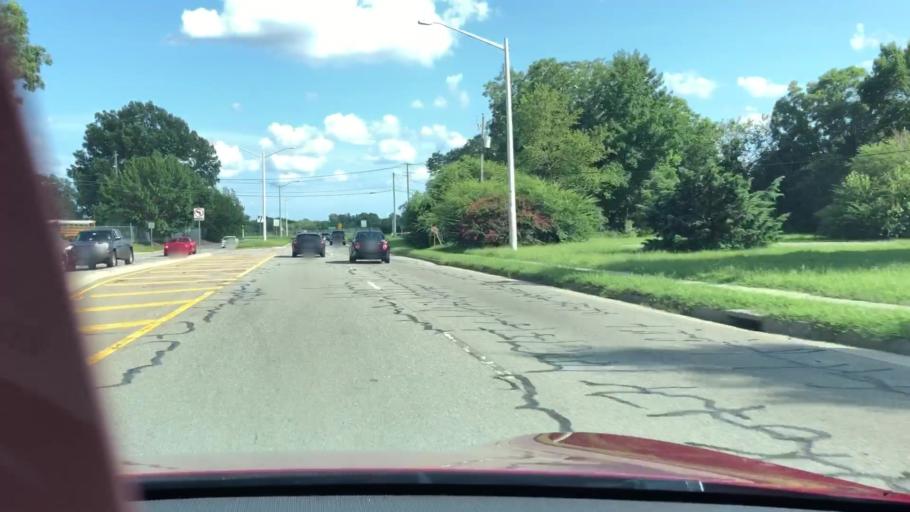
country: US
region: Virginia
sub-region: City of Virginia Beach
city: Virginia Beach
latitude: 36.8397
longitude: -76.0204
